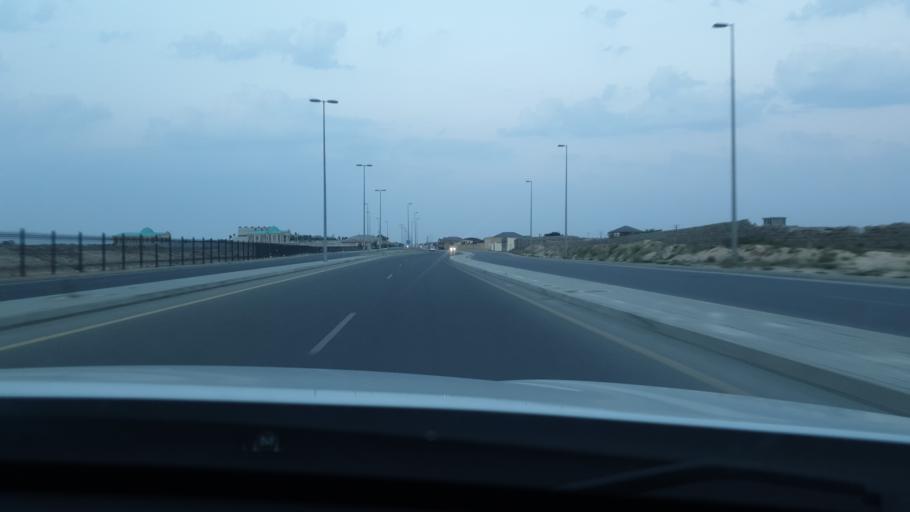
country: AZ
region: Baki
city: Nardaran
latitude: 40.5824
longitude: 50.0088
